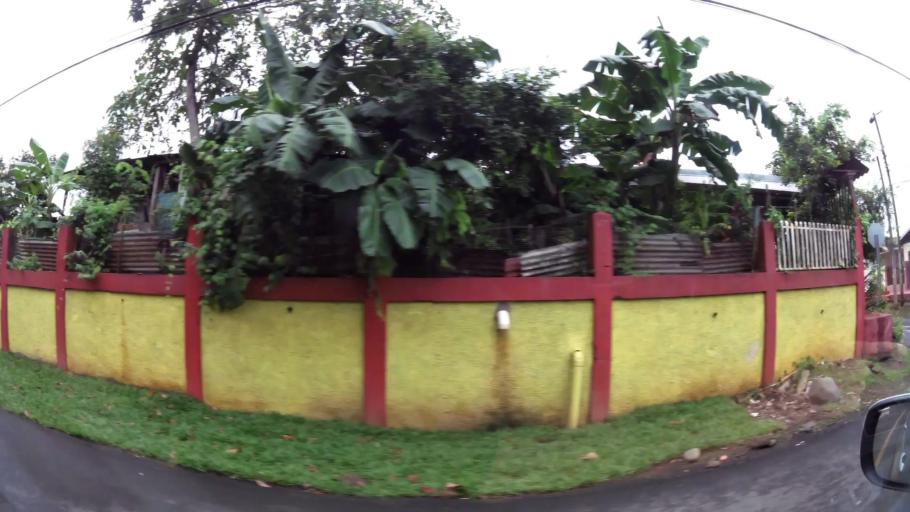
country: CR
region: Puntarenas
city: Esparza
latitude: 9.9941
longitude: -84.6665
